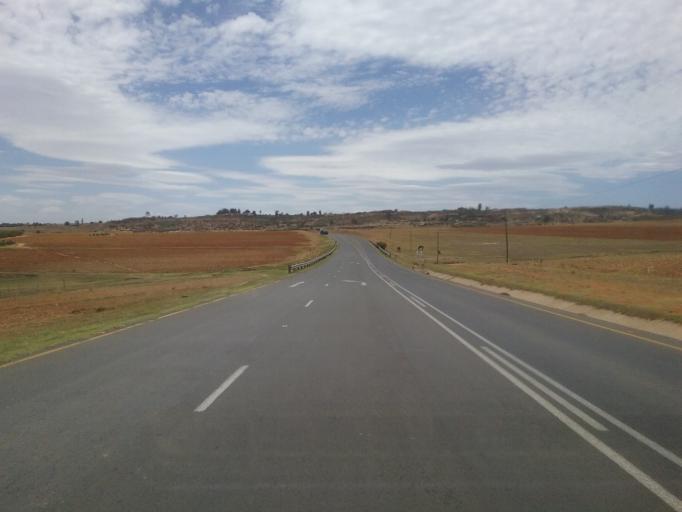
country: LS
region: Maseru
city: Maseru
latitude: -29.5081
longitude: 27.5250
